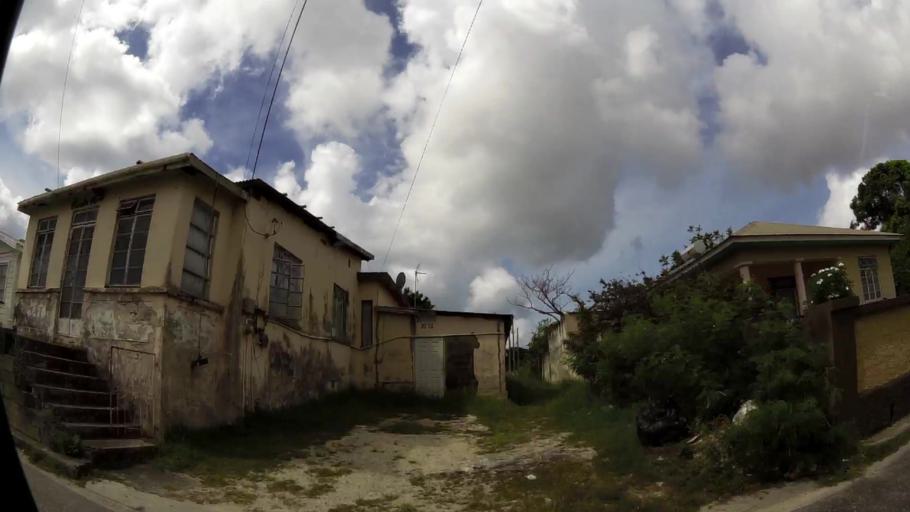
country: BB
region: Saint Michael
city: Bridgetown
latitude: 13.1201
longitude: -59.6182
